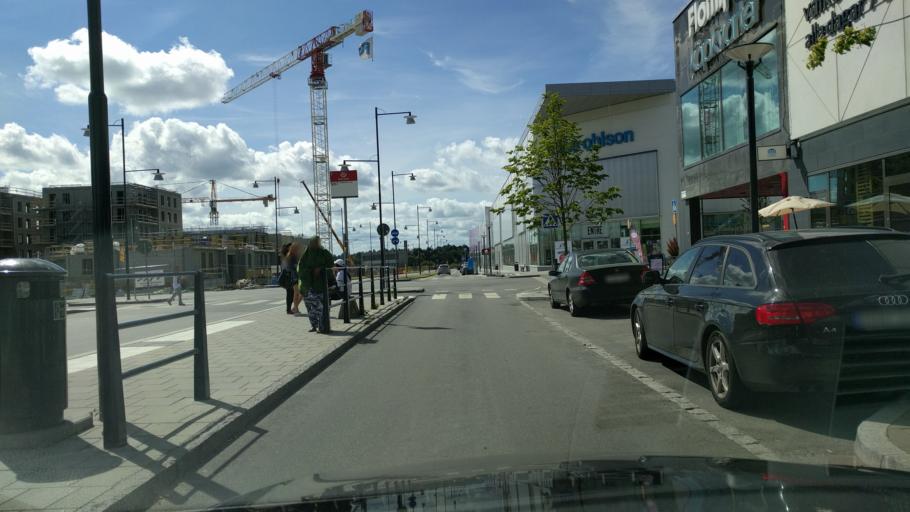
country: SE
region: Stockholm
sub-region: Jarfalla Kommun
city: Jakobsberg
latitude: 59.4137
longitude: 17.8645
